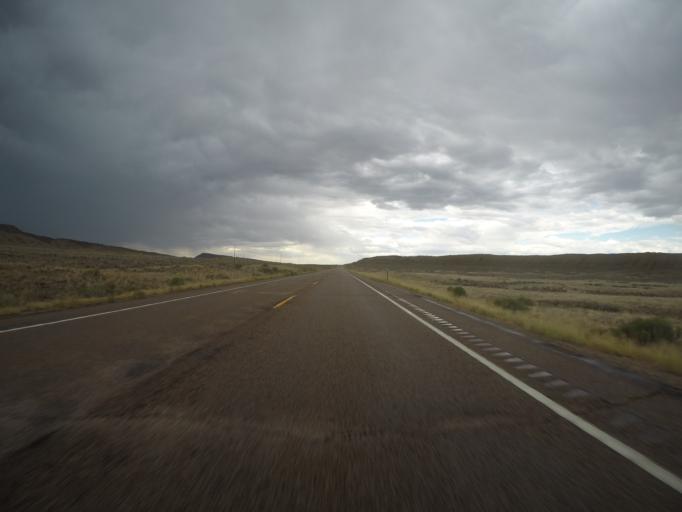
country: US
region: Colorado
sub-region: Rio Blanco County
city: Rangely
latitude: 40.2515
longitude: -108.8408
